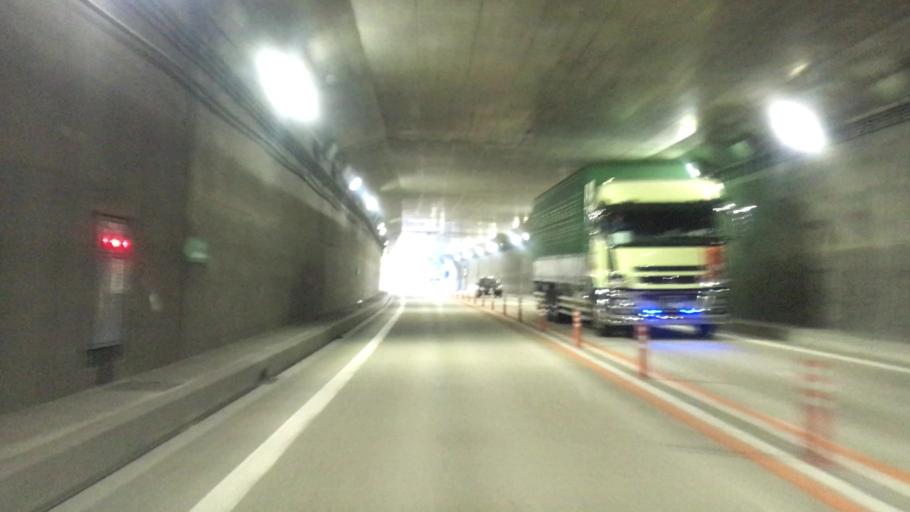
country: JP
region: Tottori
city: Tottori
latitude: 35.5521
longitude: 134.2782
